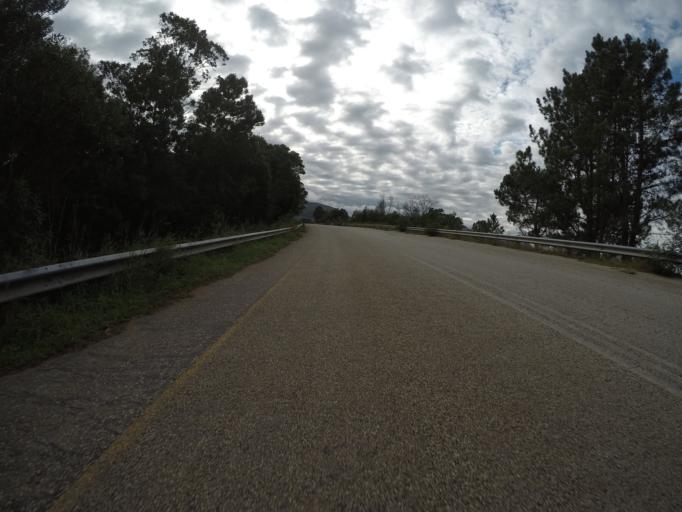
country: ZA
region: Eastern Cape
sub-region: Cacadu District Municipality
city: Kareedouw
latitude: -34.0148
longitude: 24.3051
